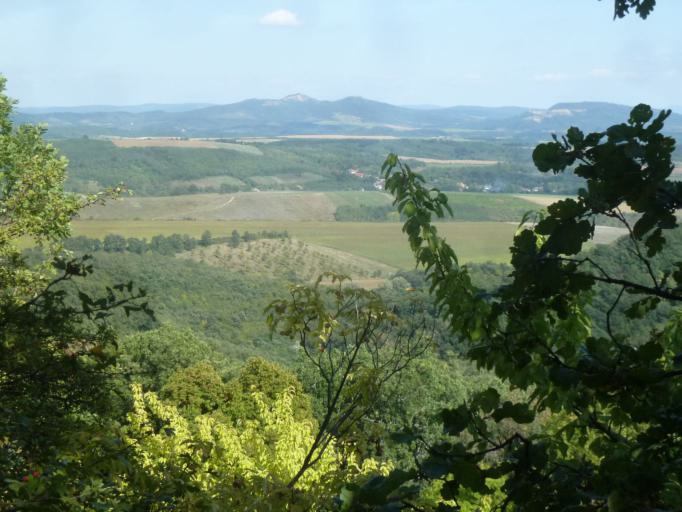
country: HU
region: Nograd
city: Romhany
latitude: 47.8713
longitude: 19.2784
